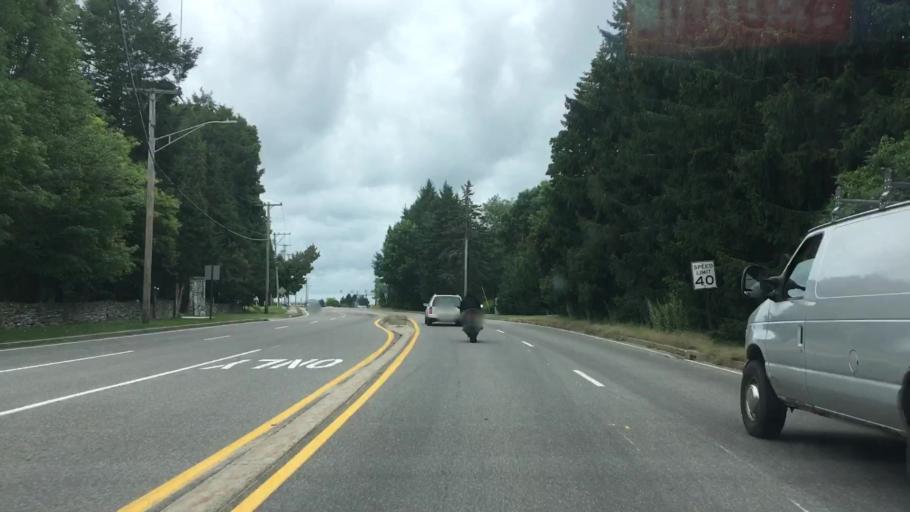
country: US
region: Maine
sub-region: Cumberland County
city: South Portland Gardens
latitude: 43.6508
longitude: -70.3236
